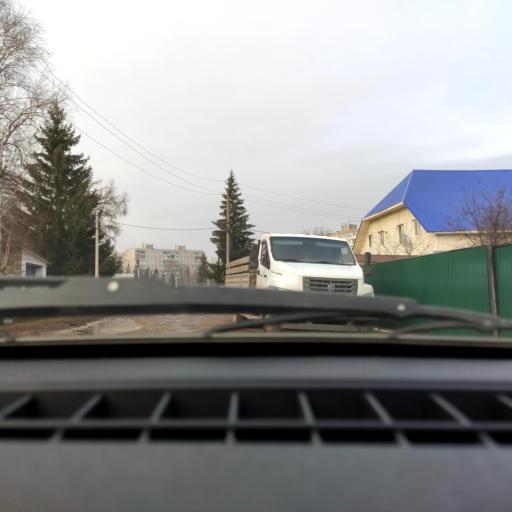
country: RU
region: Bashkortostan
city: Ufa
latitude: 54.8075
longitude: 56.1350
